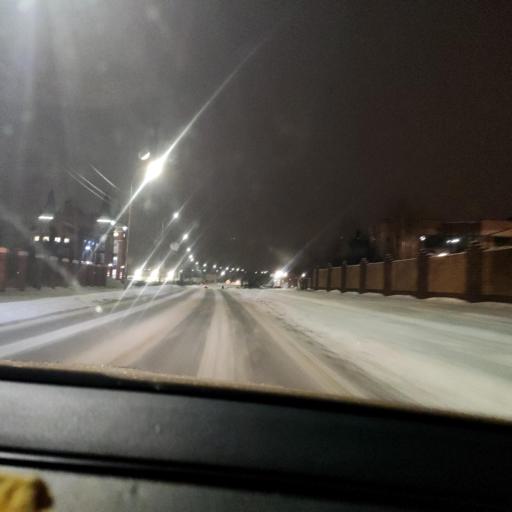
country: RU
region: Moskovskaya
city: Rozhdestveno
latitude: 55.8089
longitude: 36.9747
